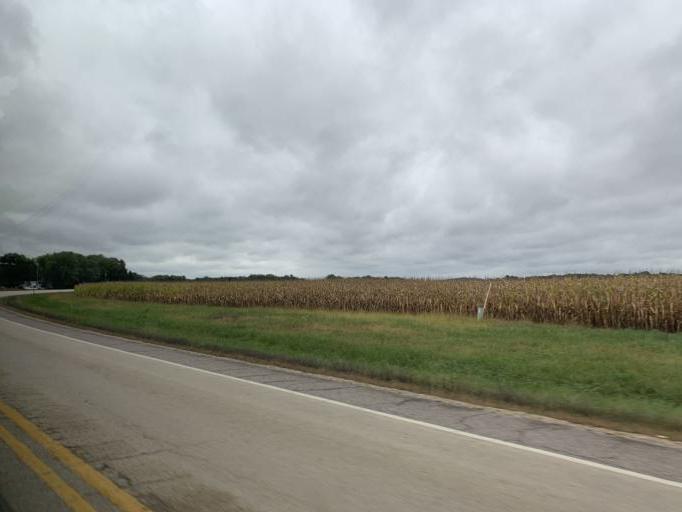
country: US
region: Wisconsin
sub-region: Sauk County
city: Sauk City
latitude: 43.2697
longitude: -89.7963
